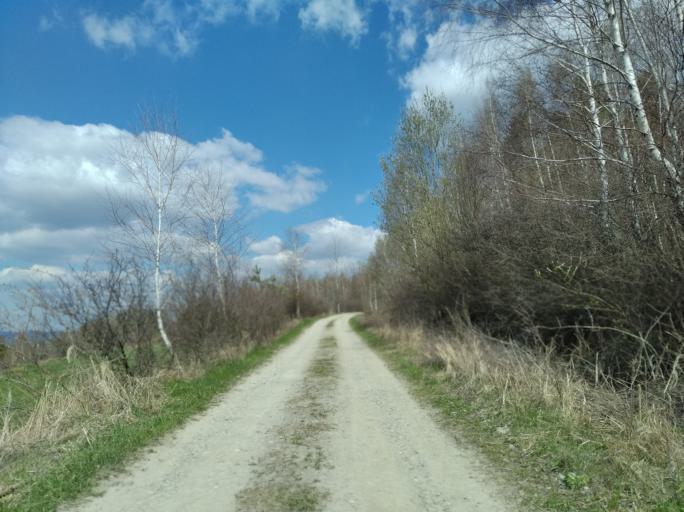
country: PL
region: Subcarpathian Voivodeship
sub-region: Powiat strzyzowski
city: Wysoka Strzyzowska
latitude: 49.8269
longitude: 21.7705
